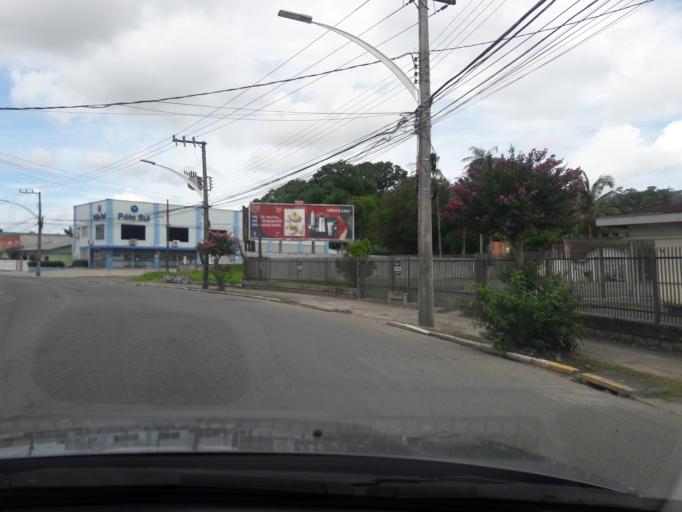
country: BR
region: Santa Catarina
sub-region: Joinville
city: Joinville
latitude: -26.3243
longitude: -48.8557
